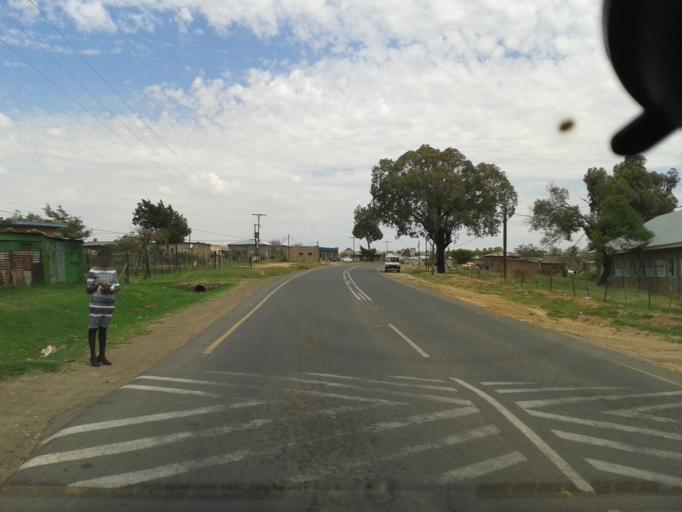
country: LS
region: Maseru
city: Maseru
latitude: -29.3536
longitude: 27.6005
